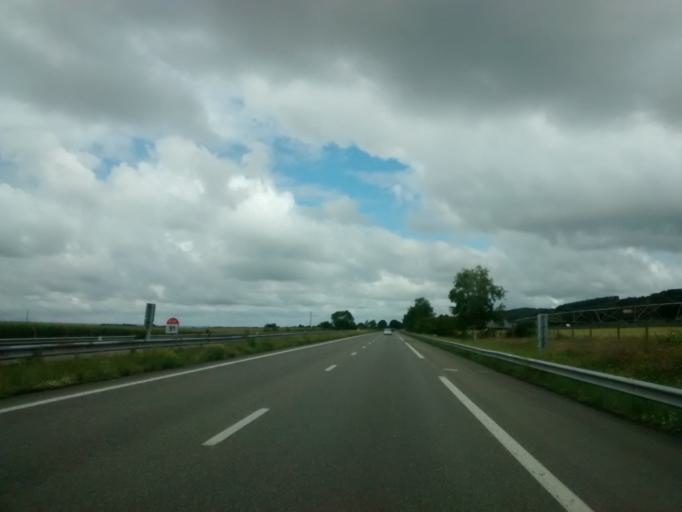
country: FR
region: Aquitaine
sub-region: Departement des Pyrenees-Atlantiques
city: Denguin
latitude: 43.3720
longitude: -0.4873
